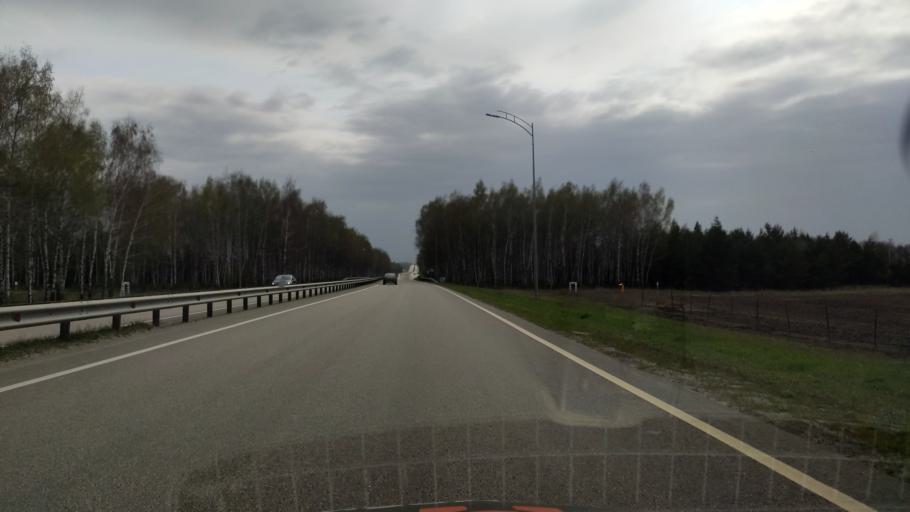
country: RU
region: Belgorod
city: Staryy Oskol
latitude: 51.4130
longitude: 37.8851
